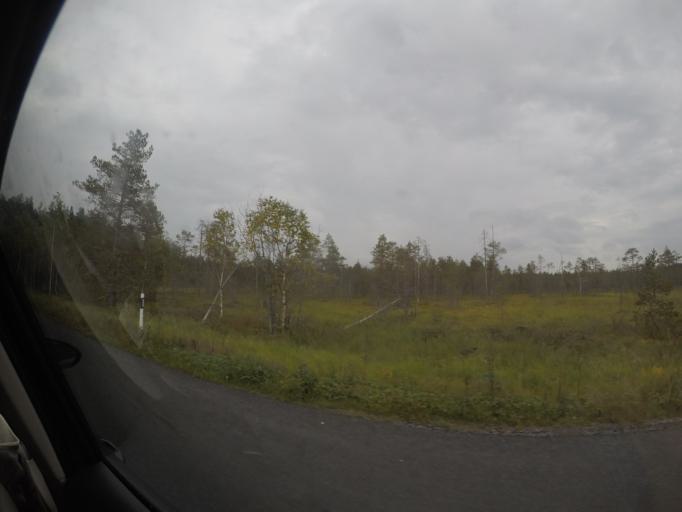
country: FI
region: Pirkanmaa
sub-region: Ylae-Pirkanmaa
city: Juupajoki
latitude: 61.8398
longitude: 24.2869
